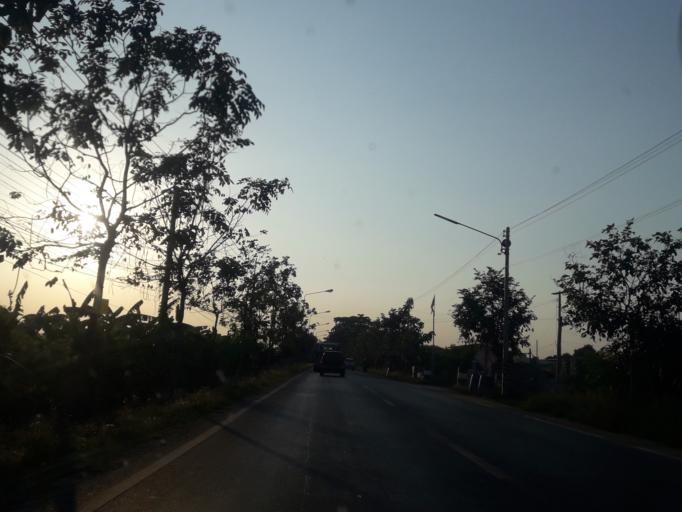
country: TH
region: Pathum Thani
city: Nong Suea
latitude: 14.1320
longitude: 100.7538
